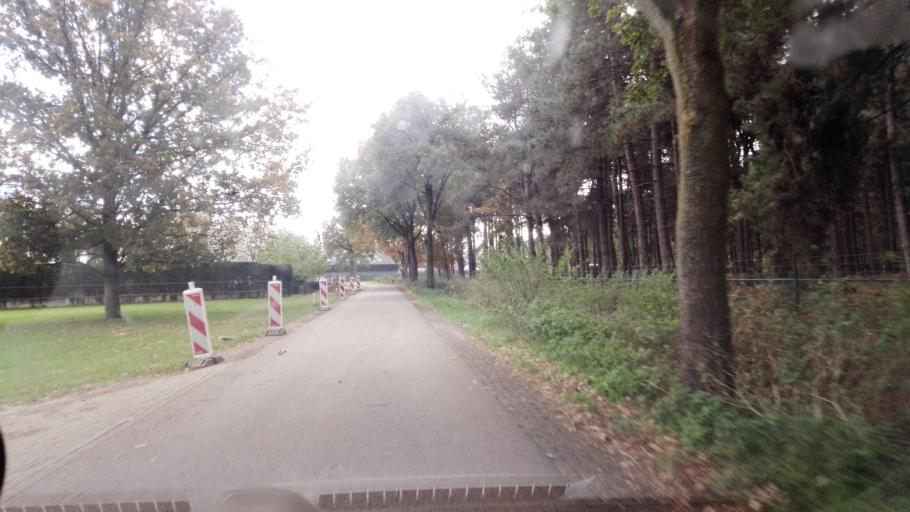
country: NL
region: Limburg
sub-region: Gemeente Venray
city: Venray
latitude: 51.4828
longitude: 5.9160
